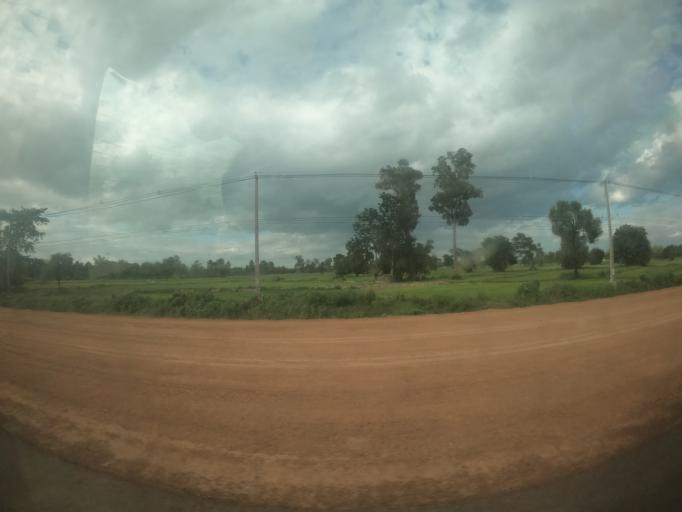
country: TH
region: Surin
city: Kap Choeng
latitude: 14.5034
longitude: 103.5604
